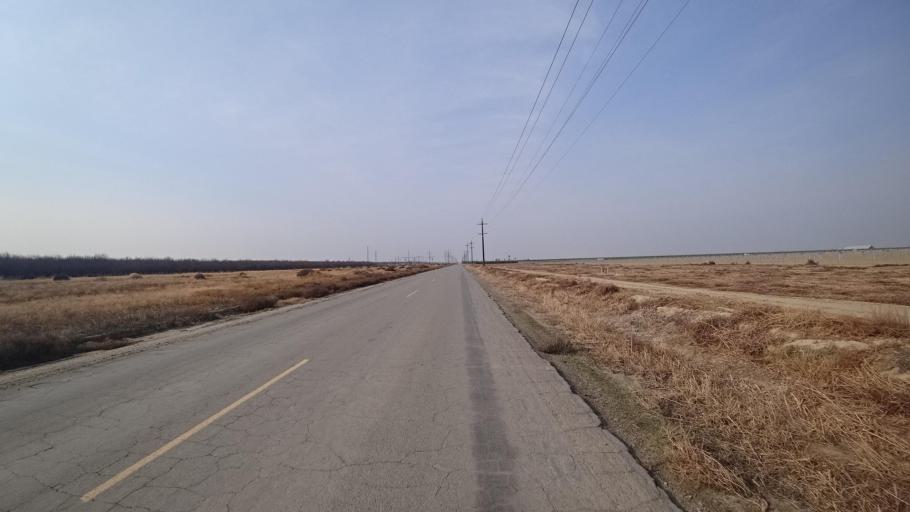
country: US
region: California
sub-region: Kern County
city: Greenfield
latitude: 35.0947
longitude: -119.0958
